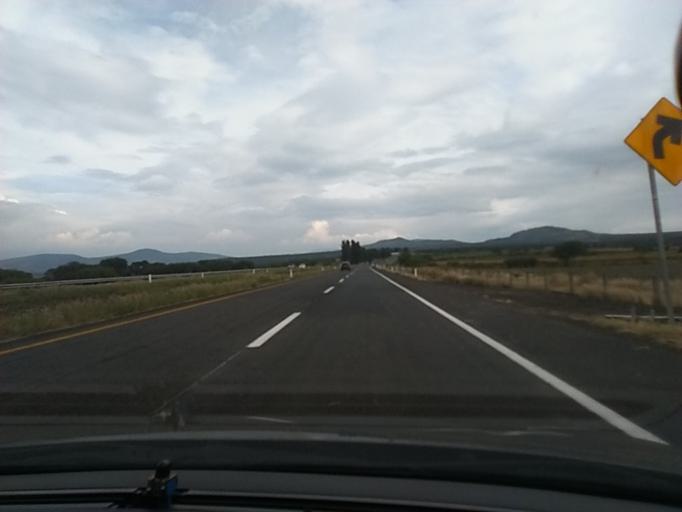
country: MX
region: Michoacan
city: Vistahermosa de Negrete
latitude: 20.2558
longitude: -102.4223
